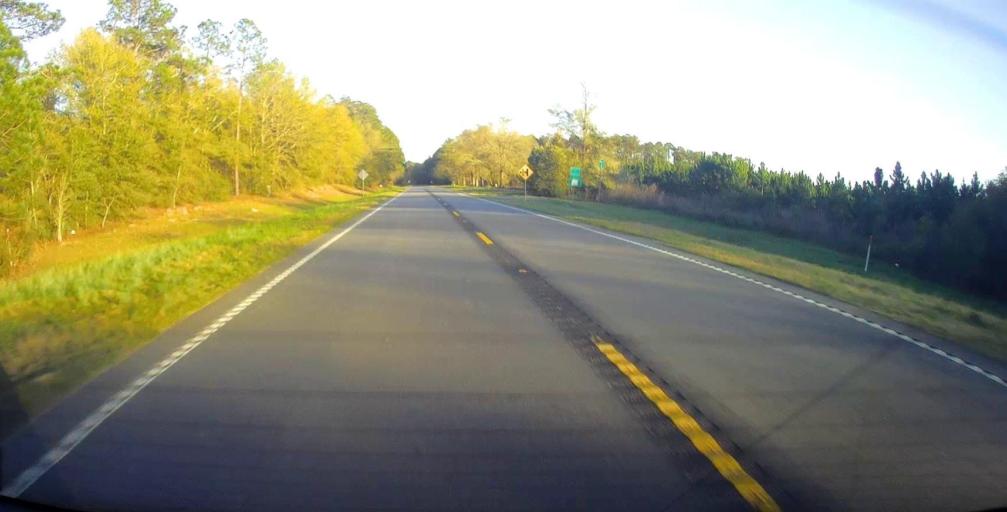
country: US
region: Georgia
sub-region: Wilcox County
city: Rochelle
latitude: 31.9554
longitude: -83.5794
